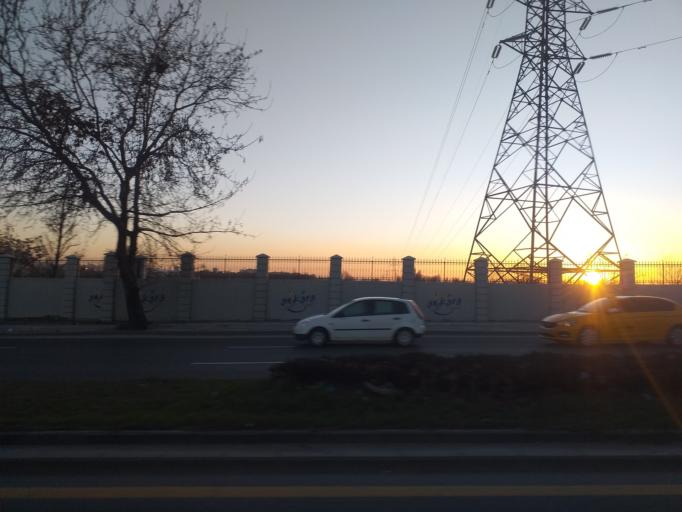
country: TR
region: Ankara
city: Ankara
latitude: 39.9523
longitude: 32.8224
